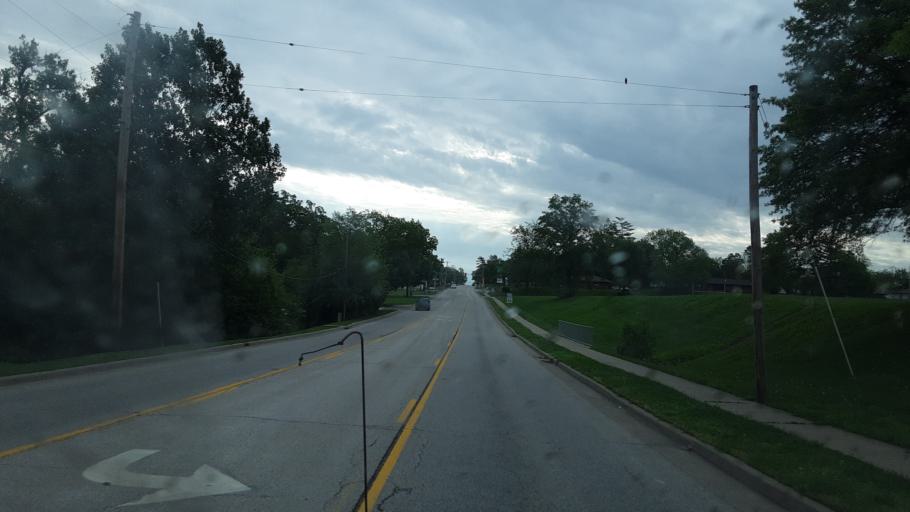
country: US
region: Illinois
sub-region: Hancock County
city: Hamilton
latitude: 40.3965
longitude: -91.3433
